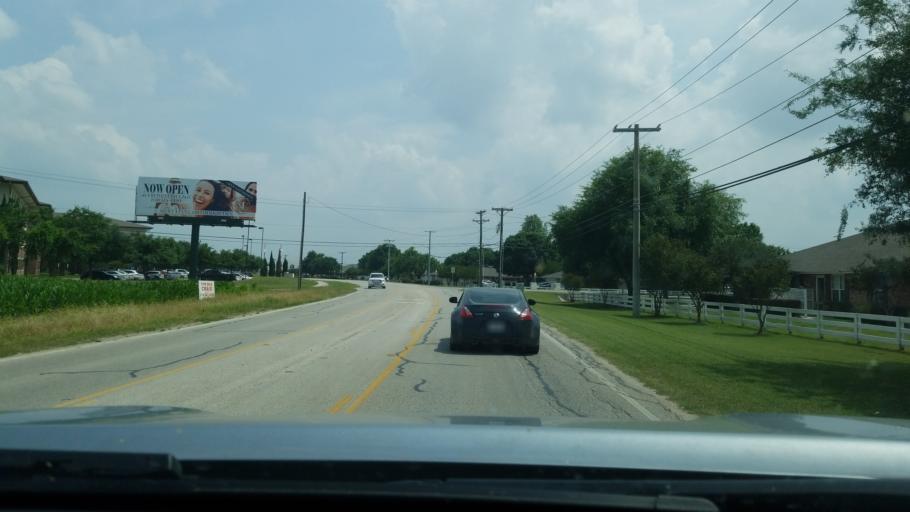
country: US
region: Texas
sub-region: Comal County
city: New Braunfels
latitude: 29.7349
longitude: -98.0987
